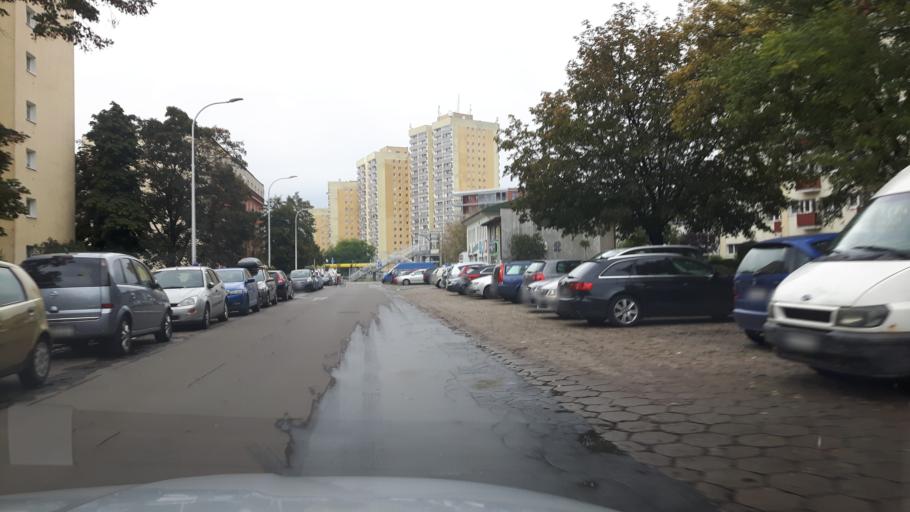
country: PL
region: Masovian Voivodeship
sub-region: Warszawa
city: Praga Poludnie
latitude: 52.2463
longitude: 21.0913
